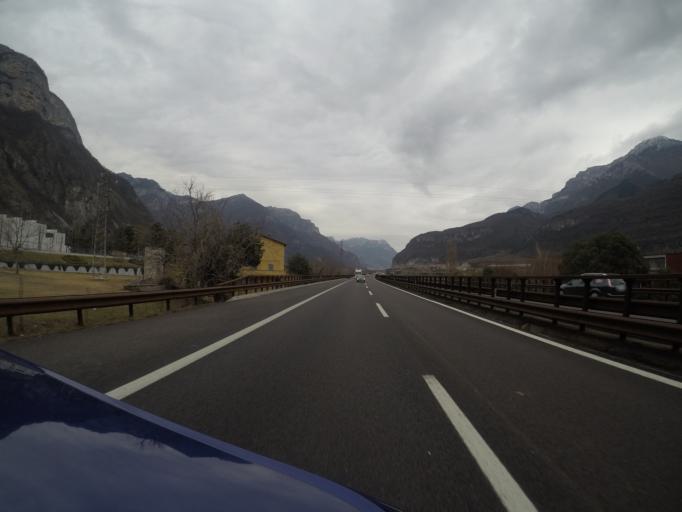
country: IT
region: Veneto
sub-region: Provincia di Verona
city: Rivalta
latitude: 45.6643
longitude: 10.8954
